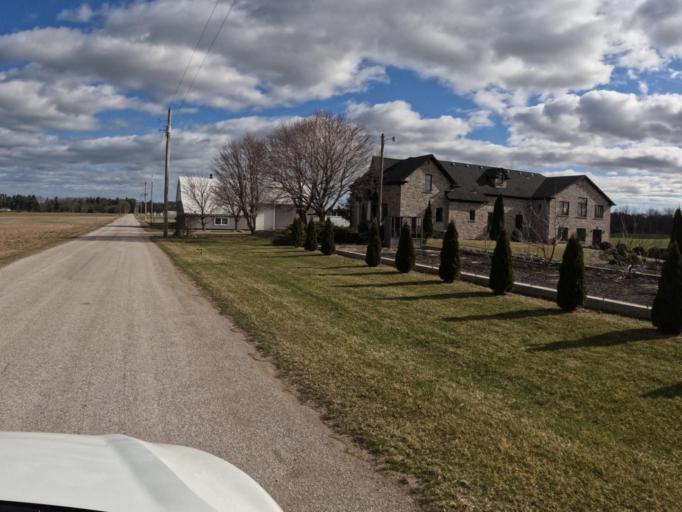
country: CA
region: Ontario
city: Norfolk County
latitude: 42.7477
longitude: -80.3840
